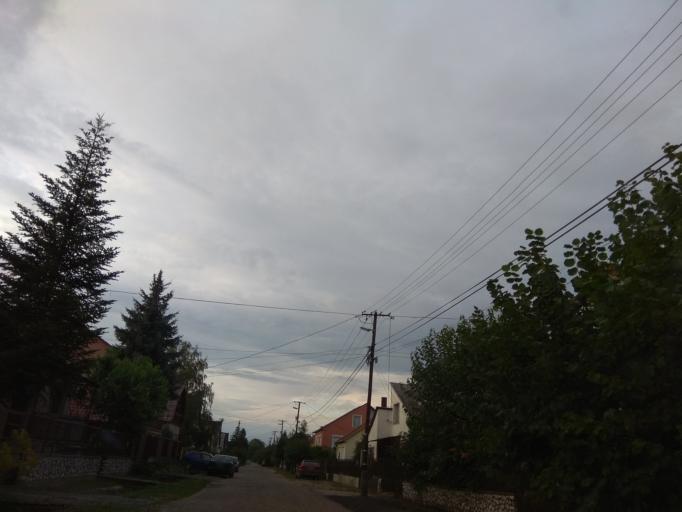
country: HU
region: Borsod-Abauj-Zemplen
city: Miskolc
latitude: 48.0597
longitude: 20.7876
